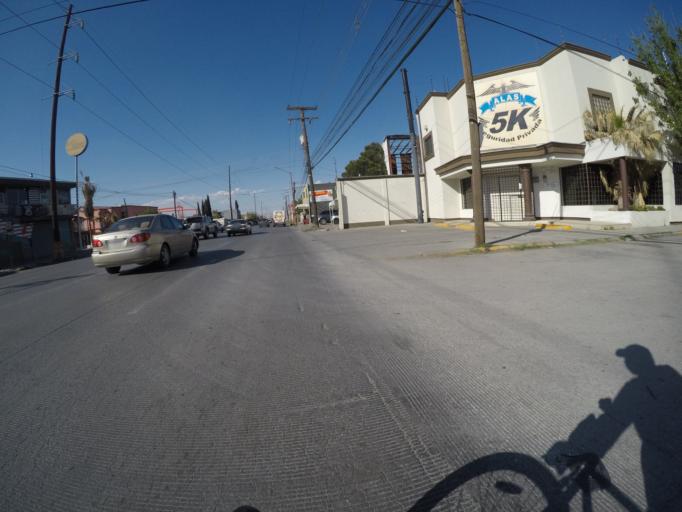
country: MX
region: Chihuahua
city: Ciudad Juarez
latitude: 31.7150
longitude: -106.4450
